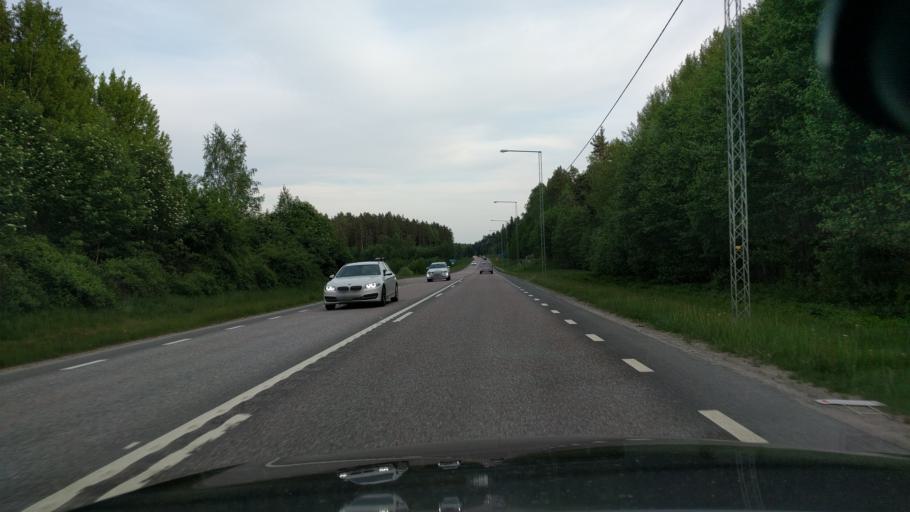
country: SE
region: Stockholm
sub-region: Vallentuna Kommun
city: Vallentuna
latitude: 59.5057
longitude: 18.0991
